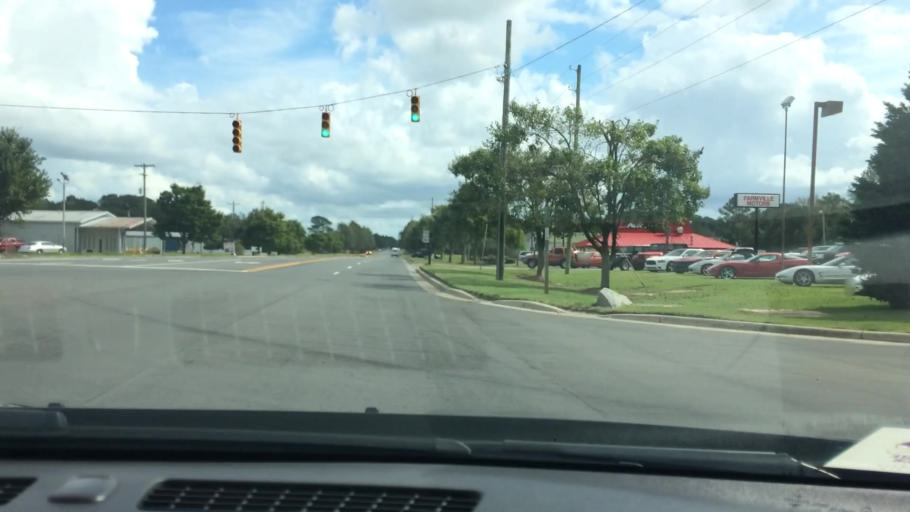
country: US
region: North Carolina
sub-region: Pitt County
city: Farmville
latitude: 35.5871
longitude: -77.6059
